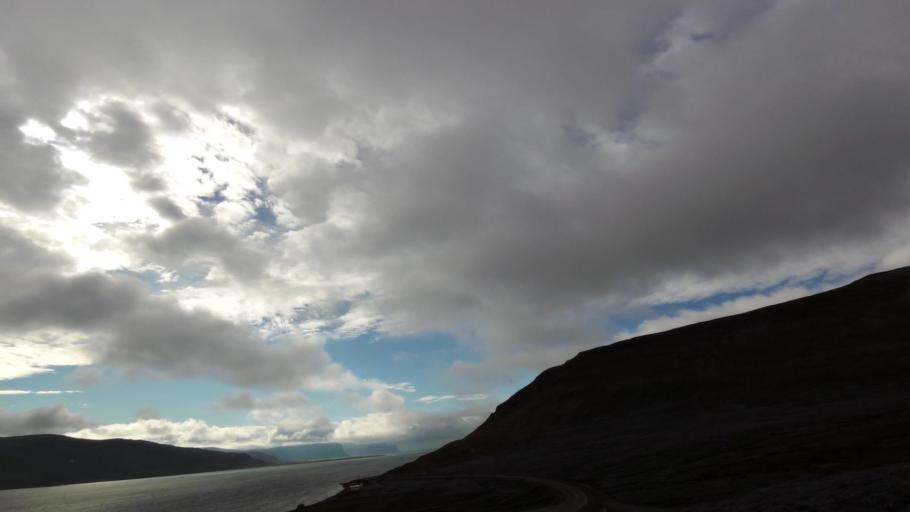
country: IS
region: West
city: Olafsvik
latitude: 65.5412
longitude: -23.8696
